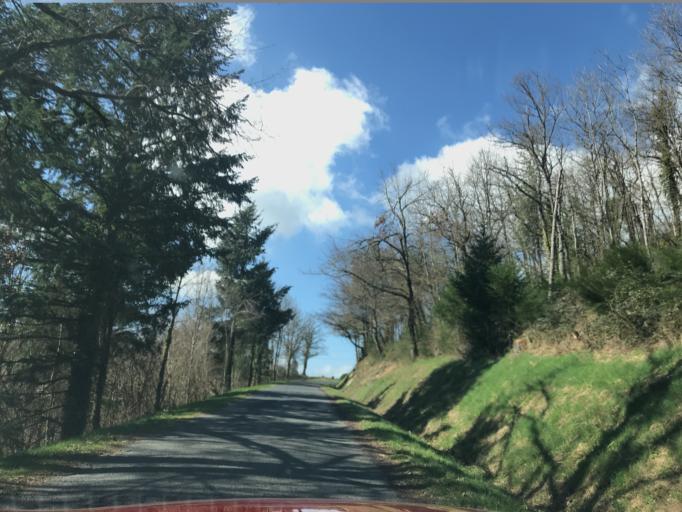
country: FR
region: Auvergne
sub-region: Departement du Puy-de-Dome
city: Escoutoux
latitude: 45.8063
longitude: 3.6031
